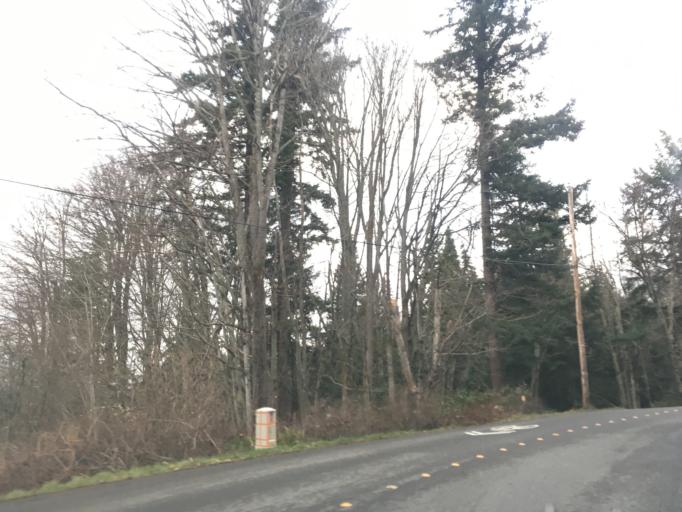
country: US
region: Washington
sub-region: Whatcom County
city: Bellingham
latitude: 48.7317
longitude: -122.4645
